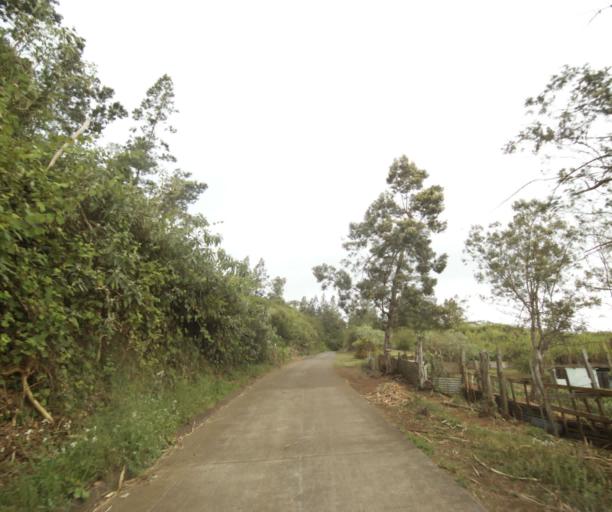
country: RE
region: Reunion
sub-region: Reunion
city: Saint-Paul
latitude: -21.0142
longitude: 55.3539
